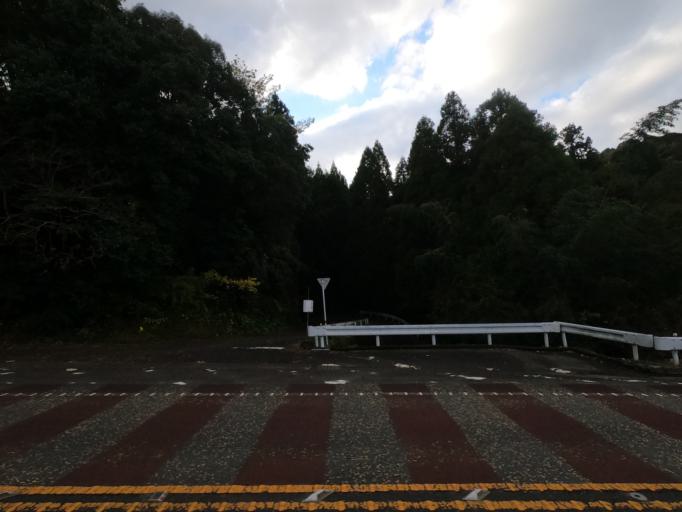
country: JP
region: Kumamoto
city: Minamata
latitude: 32.2503
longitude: 130.5027
